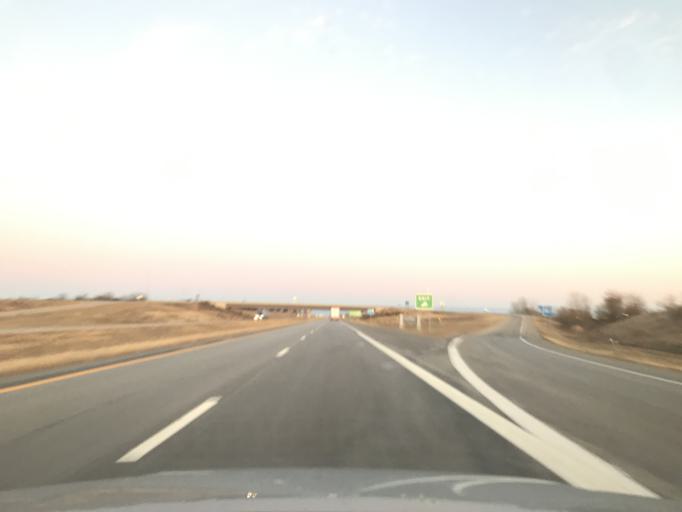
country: US
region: Missouri
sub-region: Marion County
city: Hannibal
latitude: 39.7134
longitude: -91.4498
